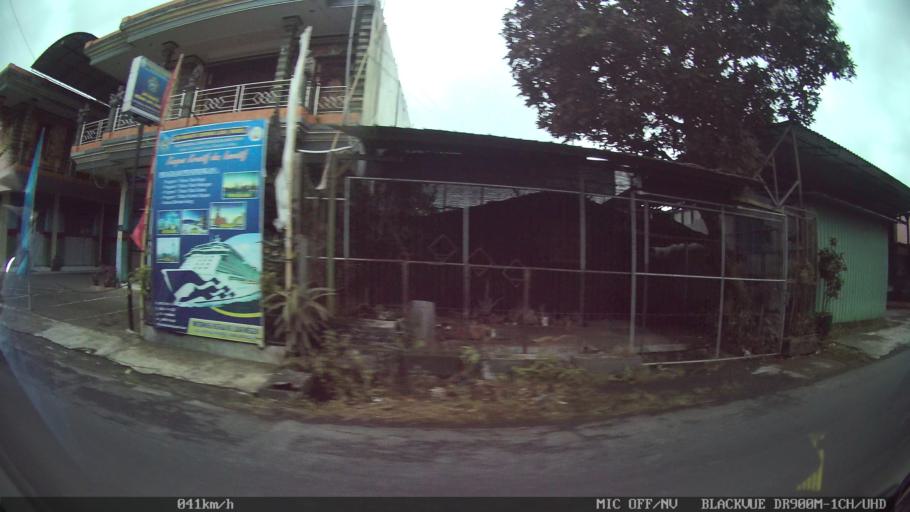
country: ID
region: Bali
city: Banjar Cemenggon
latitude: -8.5428
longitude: 115.2124
